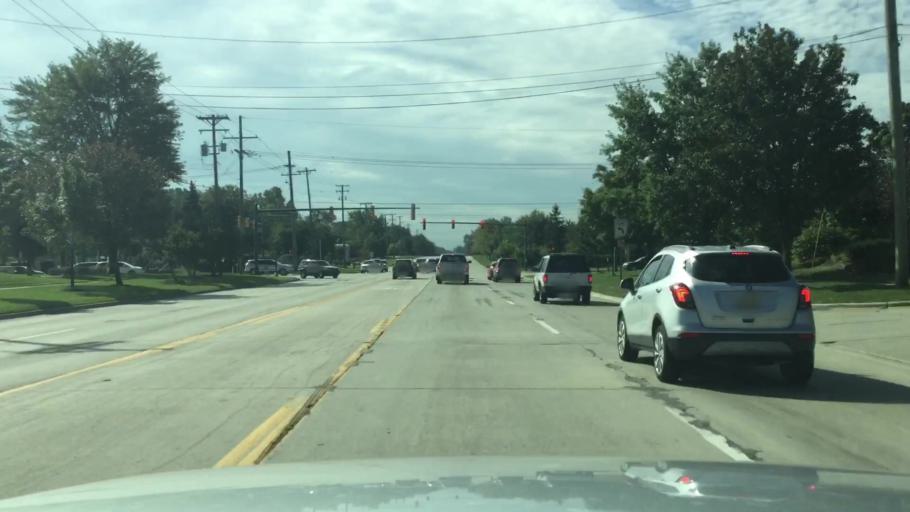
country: US
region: Michigan
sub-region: Wayne County
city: Canton
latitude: 42.3083
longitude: -83.4873
